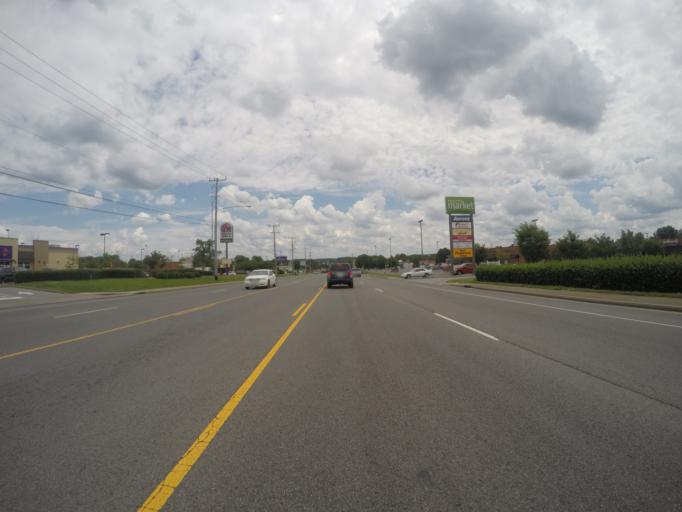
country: US
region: Tennessee
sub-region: Davidson County
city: Lakewood
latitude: 36.2151
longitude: -86.6003
